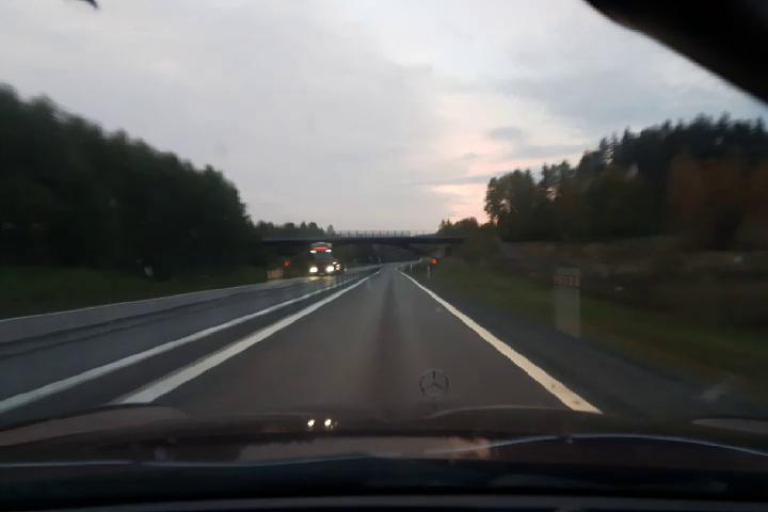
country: SE
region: Vaesternorrland
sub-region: Kramfors Kommun
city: Nordingra
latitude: 62.9376
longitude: 18.0935
